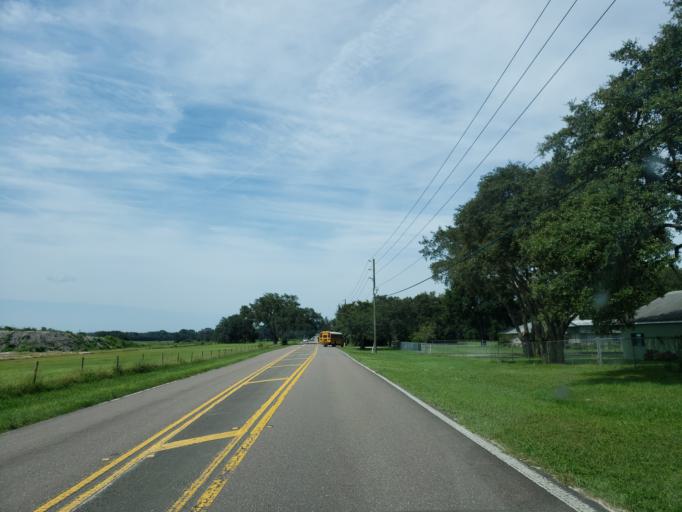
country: US
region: Florida
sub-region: Pasco County
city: San Antonio
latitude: 28.2935
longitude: -82.2787
